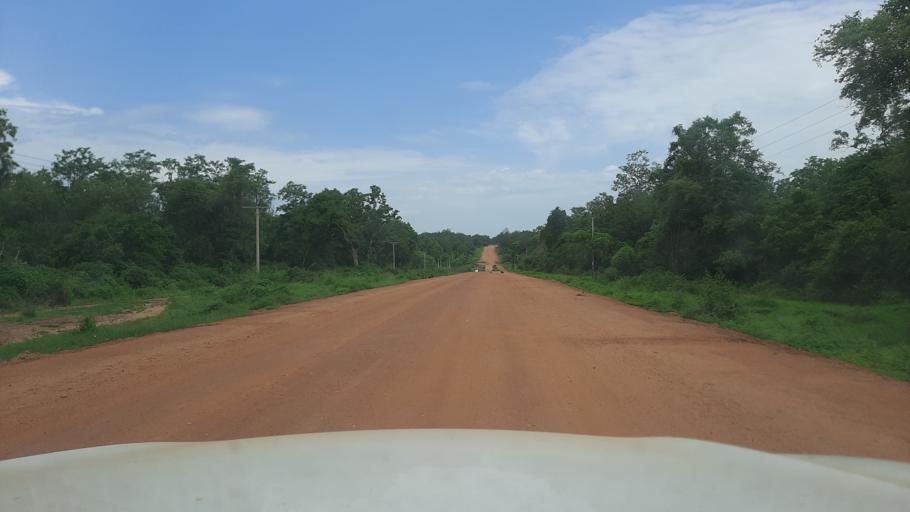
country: ET
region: Gambela
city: Gambela
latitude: 8.0924
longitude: 34.5889
